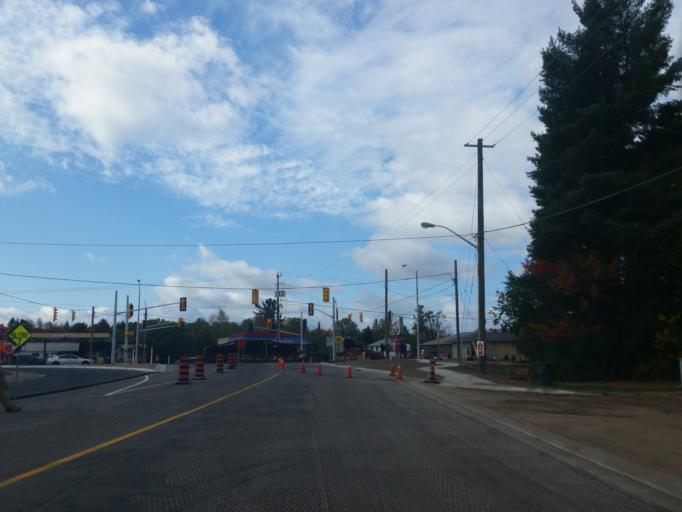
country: CA
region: Ontario
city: Deep River
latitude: 46.0982
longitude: -77.4927
